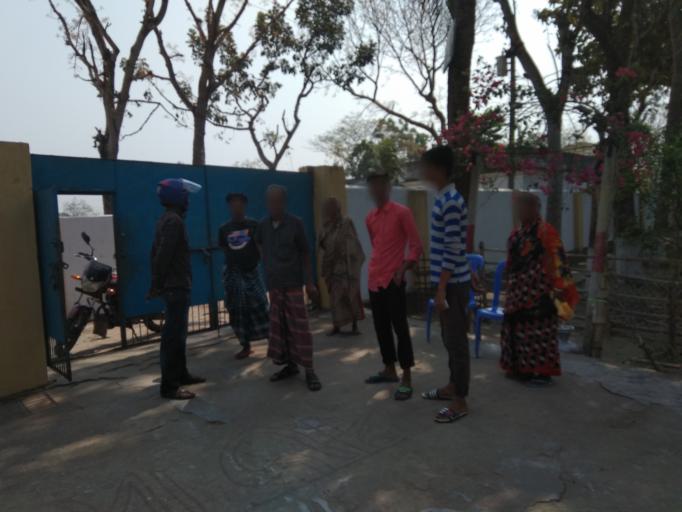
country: BD
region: Khulna
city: Satkhira
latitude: 22.5355
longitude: 89.2426
